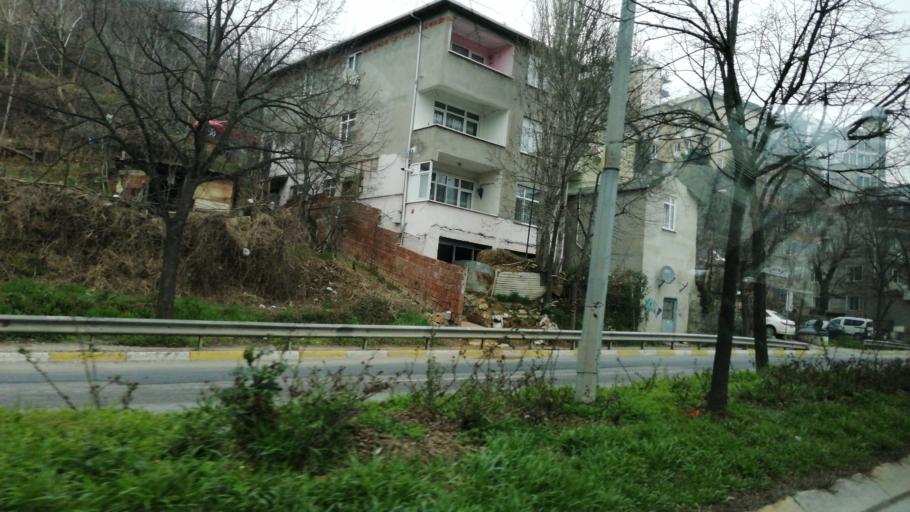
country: TR
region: Istanbul
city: Umraniye
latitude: 41.0817
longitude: 29.0813
